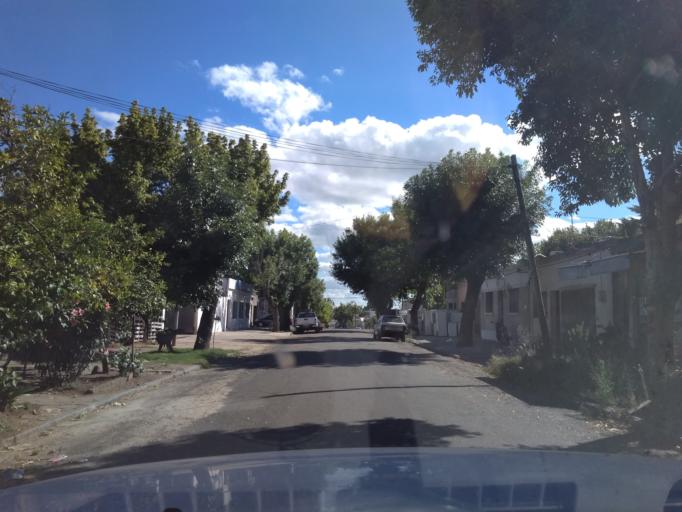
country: UY
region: Florida
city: Florida
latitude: -34.1010
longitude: -56.2081
